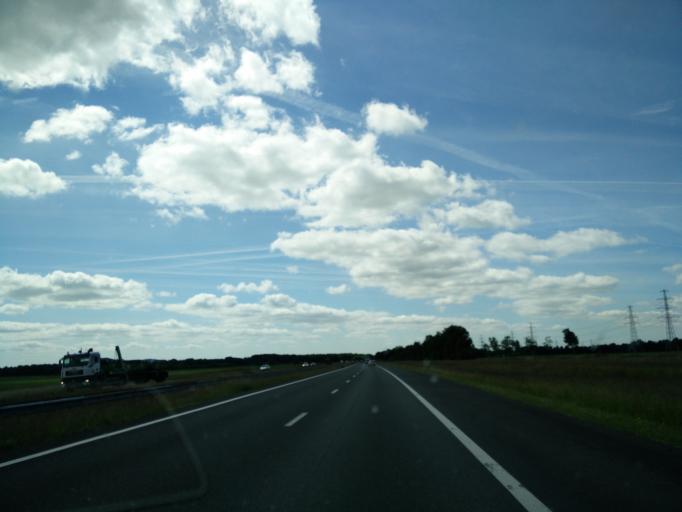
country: NL
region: Drenthe
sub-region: Gemeente Assen
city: Assen
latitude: 52.9133
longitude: 6.5308
